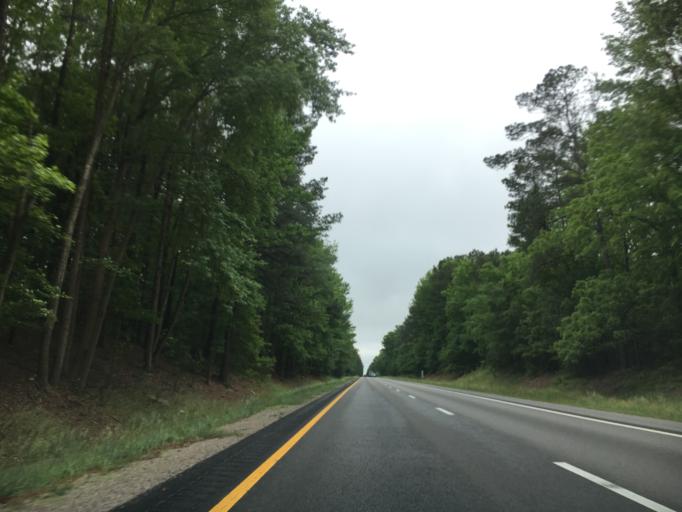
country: US
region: Virginia
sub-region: Dinwiddie County
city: Dinwiddie
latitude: 37.0439
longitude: -77.6208
